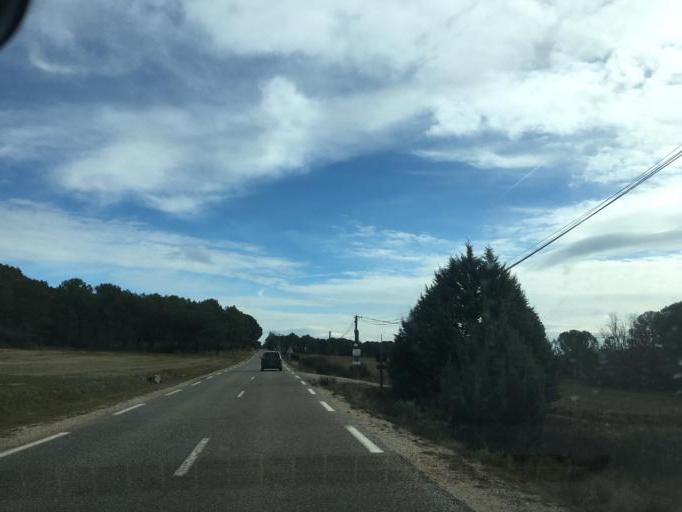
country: FR
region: Provence-Alpes-Cote d'Azur
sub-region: Departement du Var
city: La Celle
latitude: 43.4450
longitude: 6.0144
